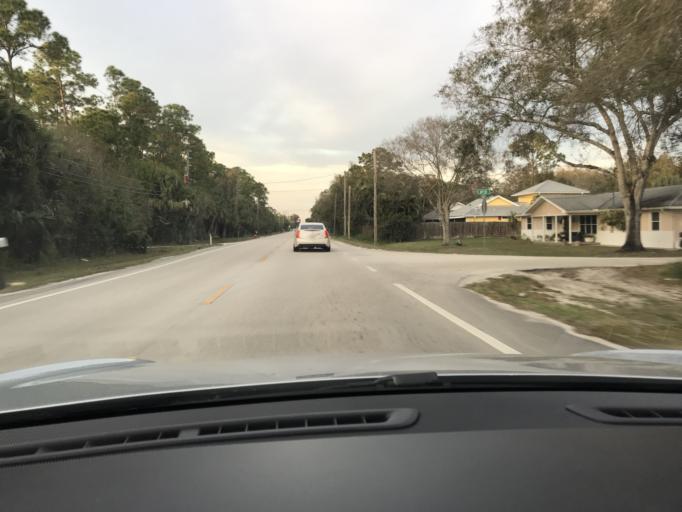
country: US
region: Florida
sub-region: Indian River County
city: Vero Beach South
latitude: 27.6126
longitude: -80.4304
